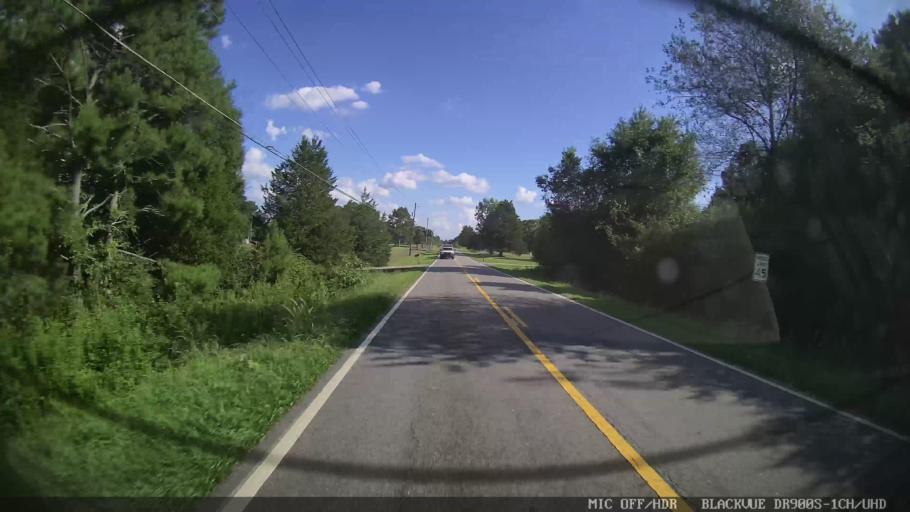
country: US
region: Georgia
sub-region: Bartow County
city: Euharlee
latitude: 34.1426
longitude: -84.9781
